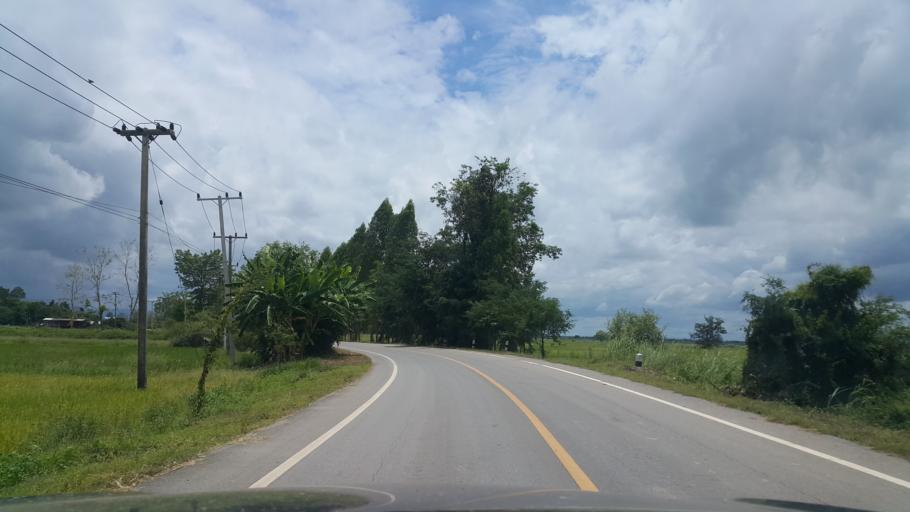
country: TH
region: Sukhothai
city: Kong Krailat
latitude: 16.9358
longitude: 99.9304
